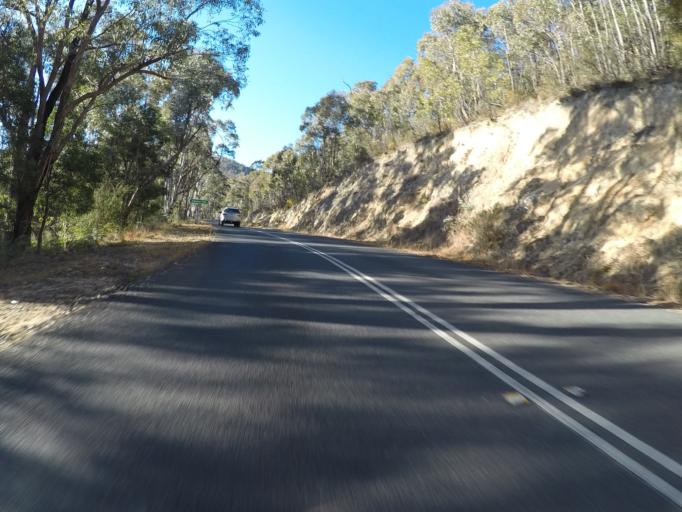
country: AU
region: Australian Capital Territory
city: Macarthur
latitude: -35.4874
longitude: 148.9317
